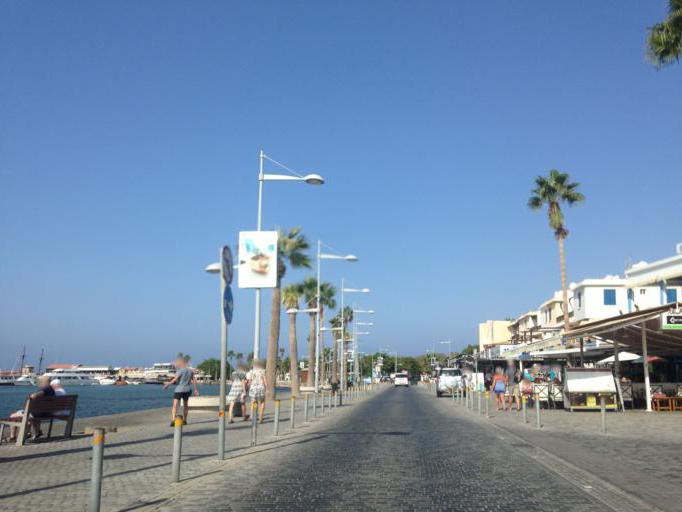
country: CY
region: Pafos
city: Paphos
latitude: 34.7554
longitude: 32.4125
